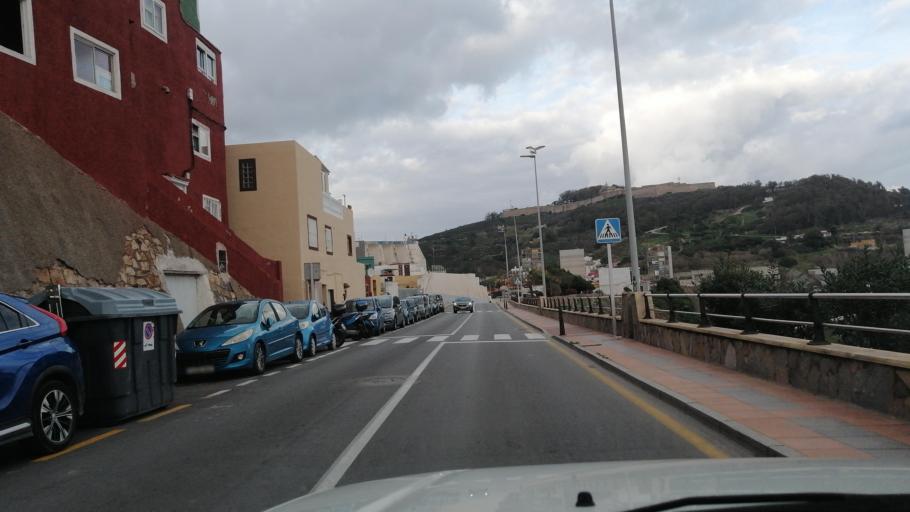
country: ES
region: Ceuta
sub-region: Ceuta
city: Ceuta
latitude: 35.8884
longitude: -5.3003
